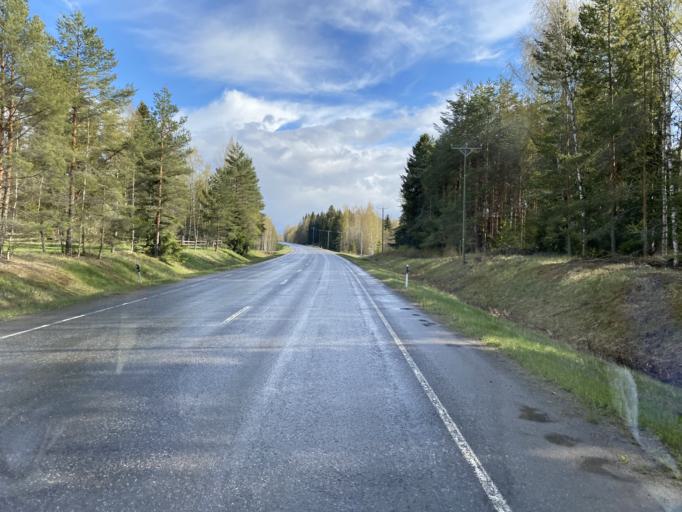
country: FI
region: Pirkanmaa
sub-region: Etelae-Pirkanmaa
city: Viiala
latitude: 61.2411
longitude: 23.7384
